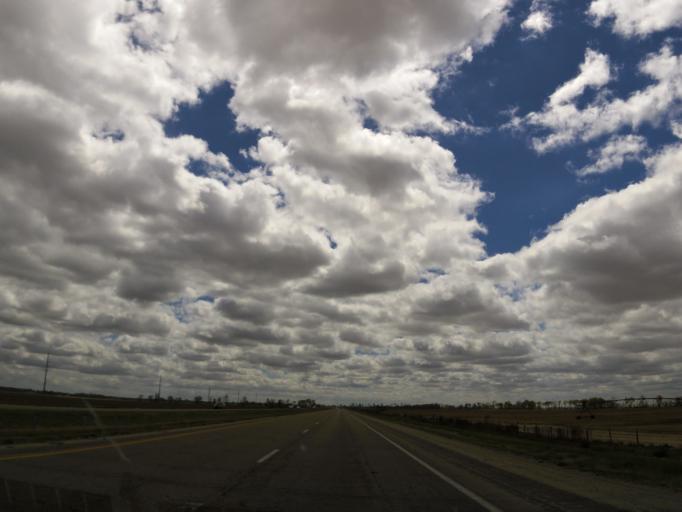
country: US
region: Arkansas
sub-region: Poinsett County
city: Trumann
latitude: 35.5958
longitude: -90.4968
